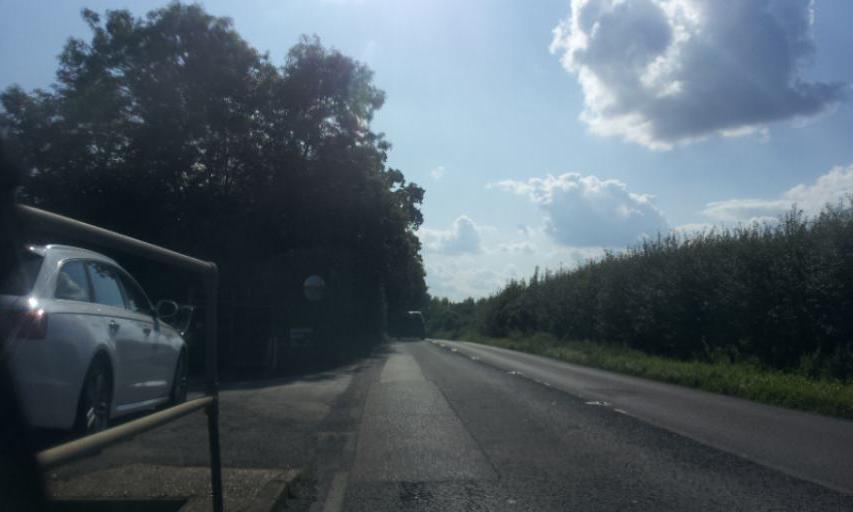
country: GB
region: England
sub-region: Kent
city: Yalding
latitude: 51.2302
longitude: 0.4051
